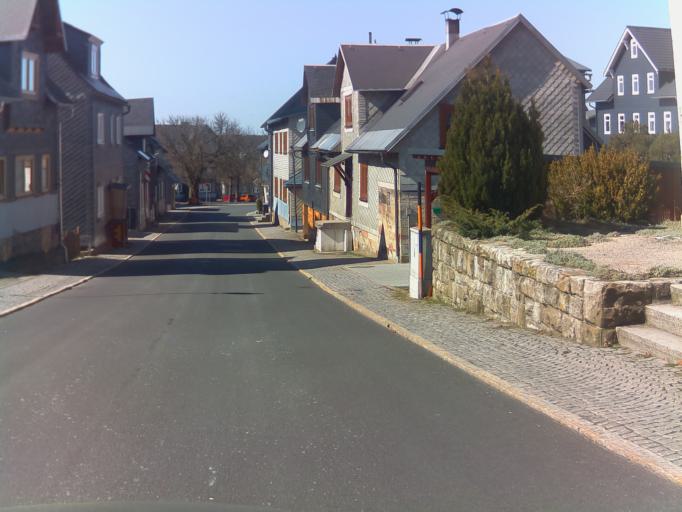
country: DE
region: Thuringia
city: Steinheid
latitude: 50.4642
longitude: 11.0837
